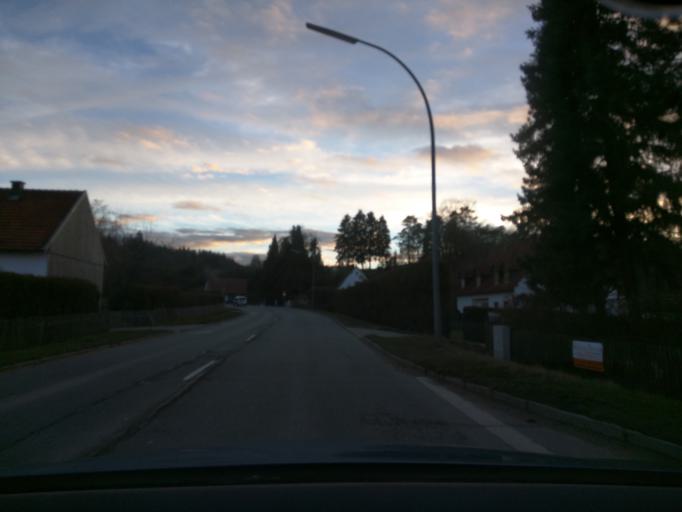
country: DE
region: Bavaria
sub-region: Upper Bavaria
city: Zolling
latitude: 48.4398
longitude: 11.7627
